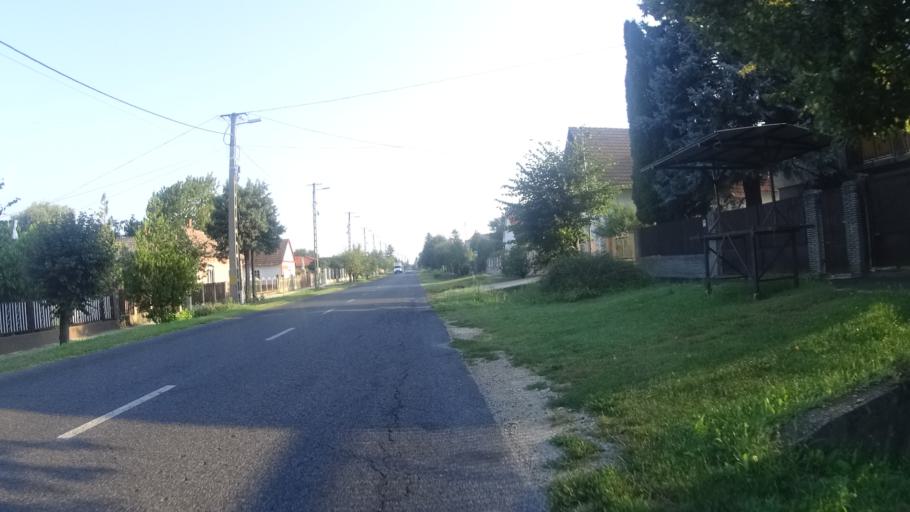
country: HU
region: Zala
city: Zalakomar
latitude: 46.5865
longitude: 17.1767
